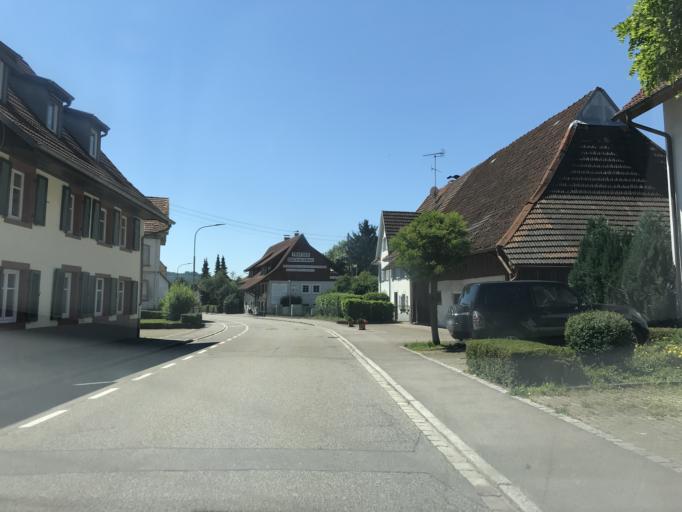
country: DE
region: Baden-Wuerttemberg
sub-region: Freiburg Region
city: Maulburg
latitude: 47.6594
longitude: 7.7990
